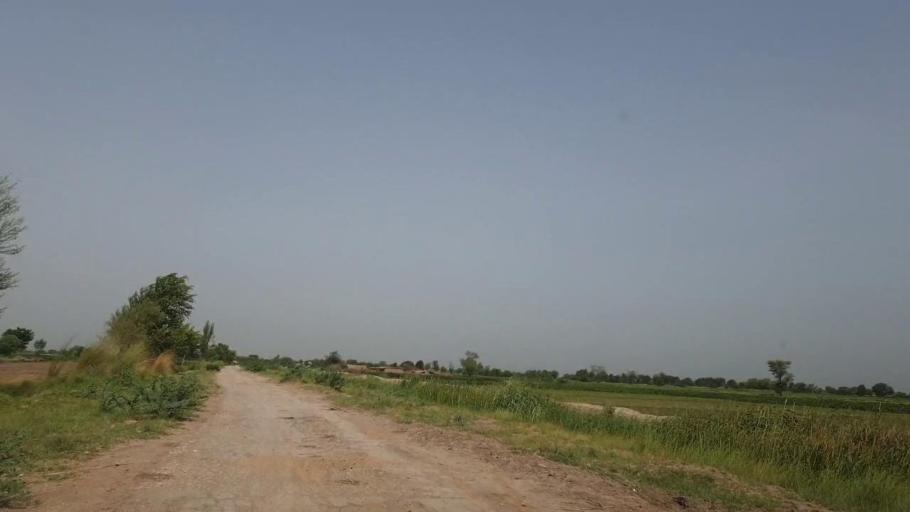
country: PK
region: Sindh
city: Sakrand
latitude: 26.1287
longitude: 68.3693
